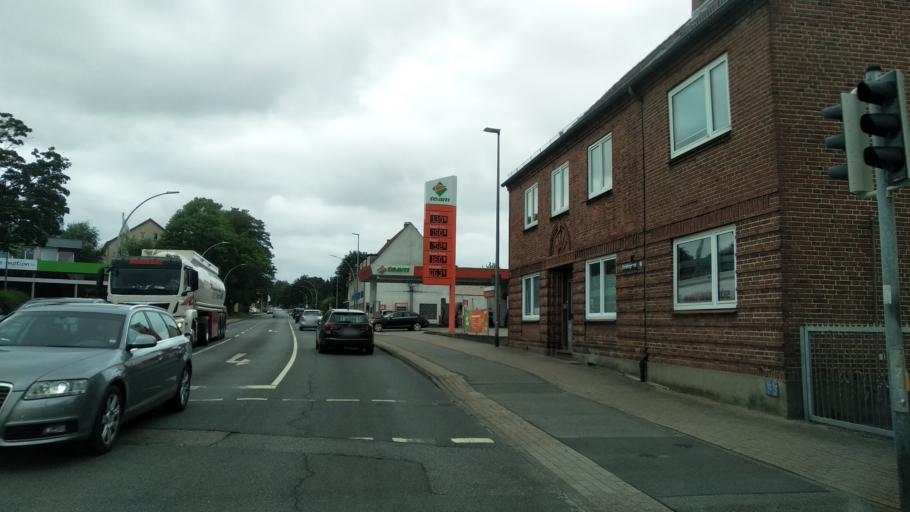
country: DE
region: Schleswig-Holstein
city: Schleswig
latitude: 54.5237
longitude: 9.5433
